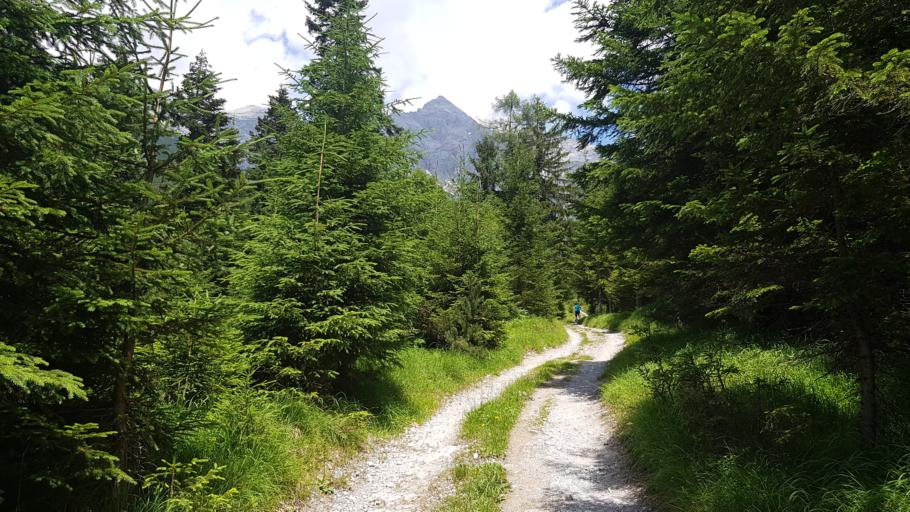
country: AT
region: Salzburg
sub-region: Politischer Bezirk Zell am See
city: Maria Alm am Steinernen Meer
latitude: 47.4333
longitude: 12.9348
